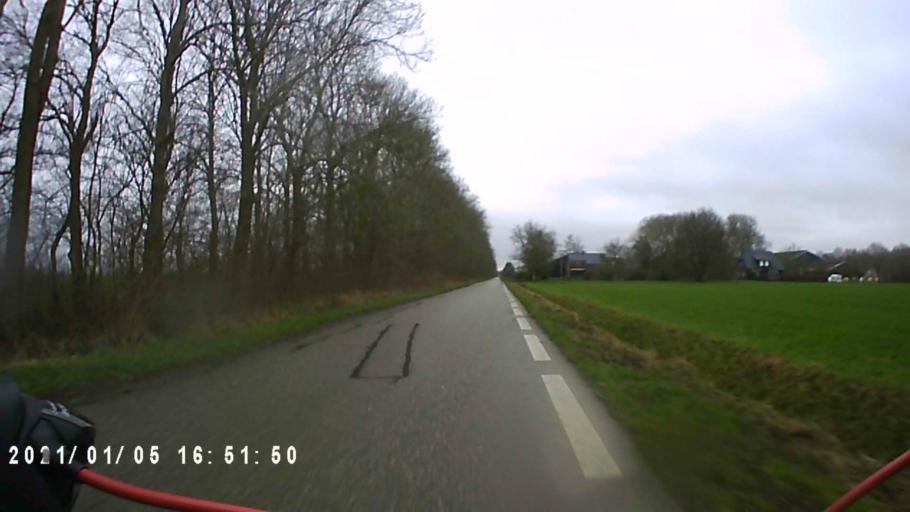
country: NL
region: Groningen
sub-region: Gemeente  Oldambt
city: Winschoten
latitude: 53.2345
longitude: 7.0596
